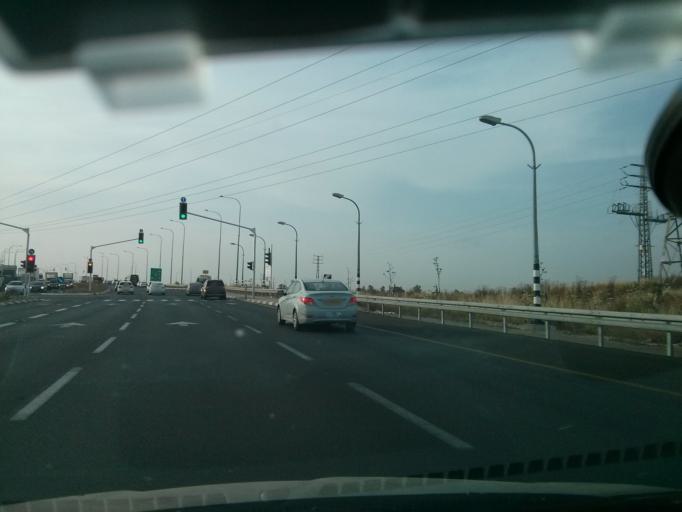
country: IL
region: Central District
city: Bene 'Ayish
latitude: 31.7963
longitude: 34.7659
